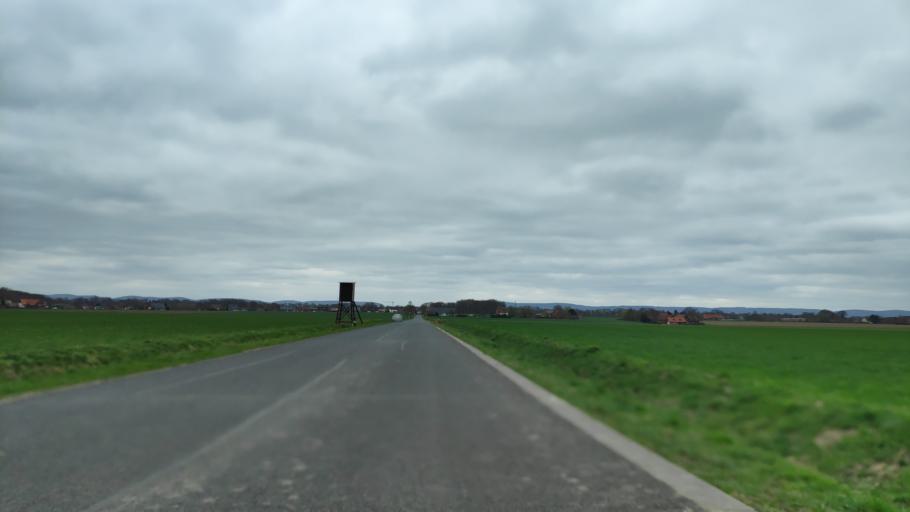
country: DE
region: North Rhine-Westphalia
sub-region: Regierungsbezirk Detmold
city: Petershagen
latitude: 52.3554
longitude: 8.9314
